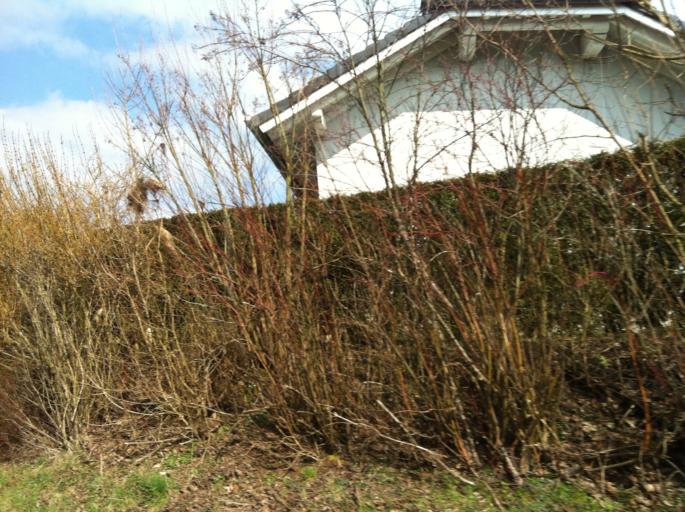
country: DE
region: Baden-Wuerttemberg
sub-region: Karlsruhe Region
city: Fahrenbach
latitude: 49.4503
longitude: 9.1621
